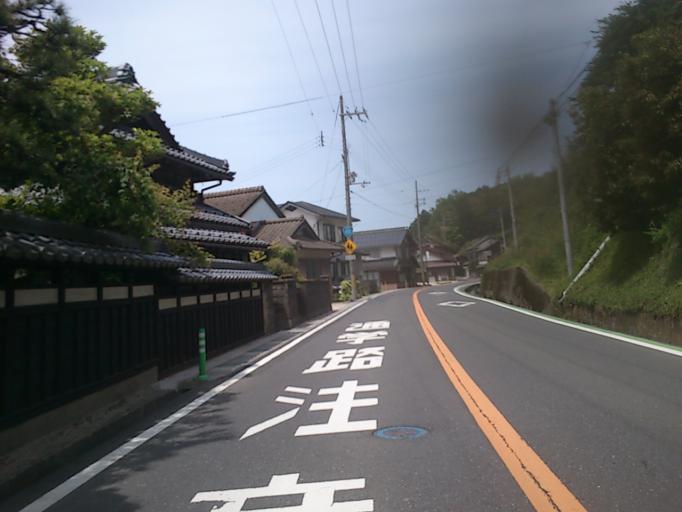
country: JP
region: Kyoto
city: Miyazu
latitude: 35.6604
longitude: 135.0925
